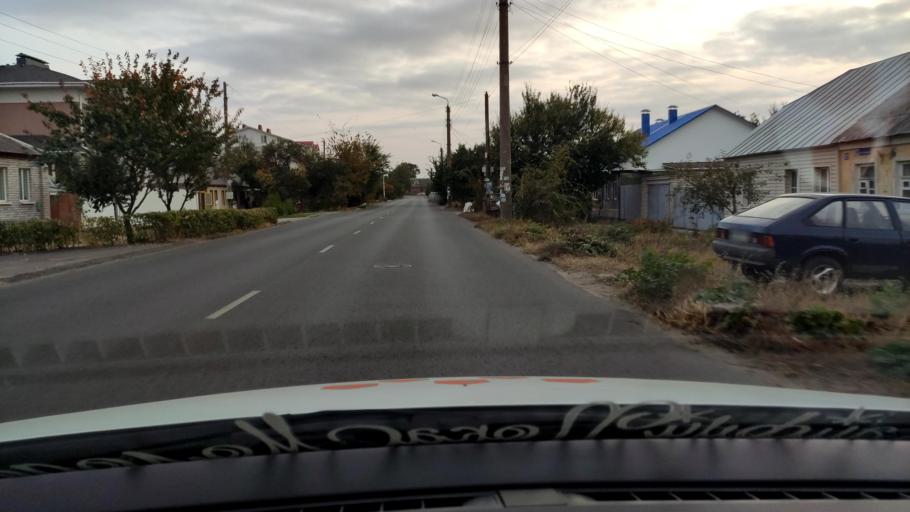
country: RU
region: Voronezj
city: Voronezh
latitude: 51.6405
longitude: 39.1690
